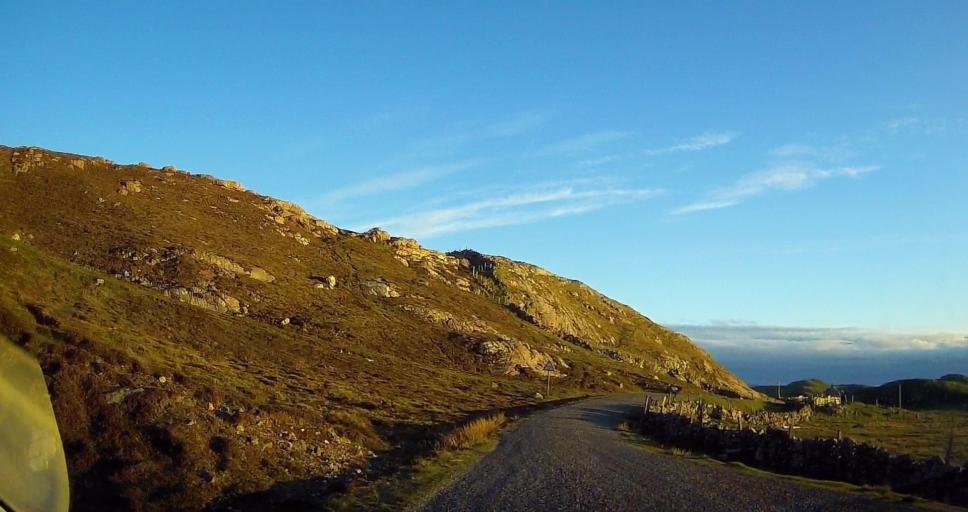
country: GB
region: Scotland
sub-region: Shetland Islands
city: Lerwick
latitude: 60.4443
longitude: -1.4420
